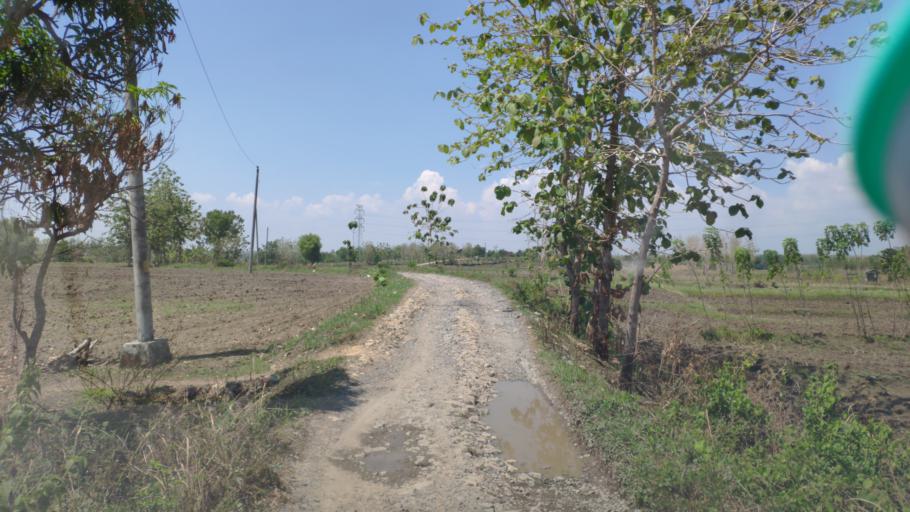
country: ID
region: Central Java
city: Galuk
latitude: -7.1030
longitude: 111.5023
